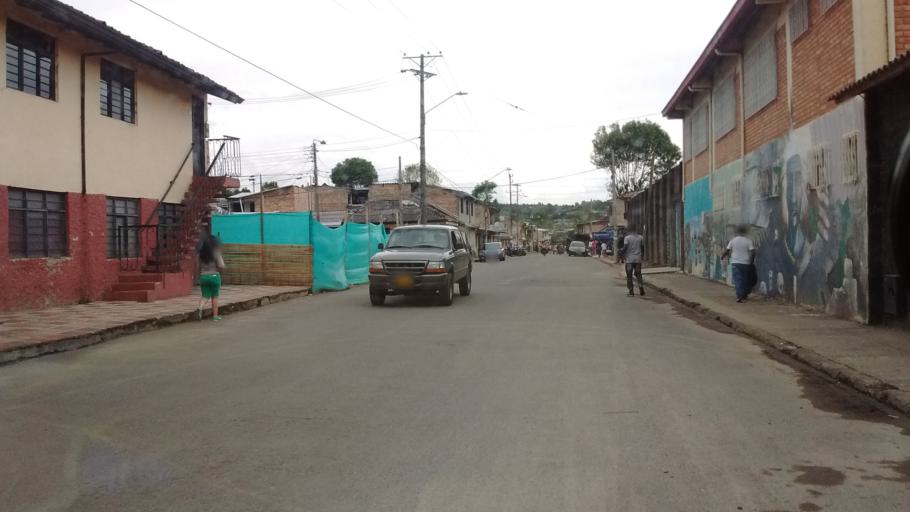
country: CO
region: Cauca
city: Popayan
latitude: 2.4340
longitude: -76.6107
